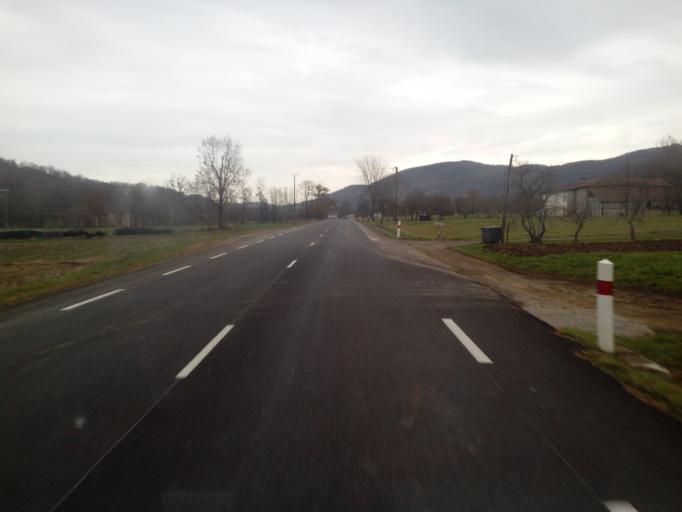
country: FR
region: Midi-Pyrenees
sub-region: Departement de l'Ariege
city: Foix
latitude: 43.0102
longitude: 1.4506
